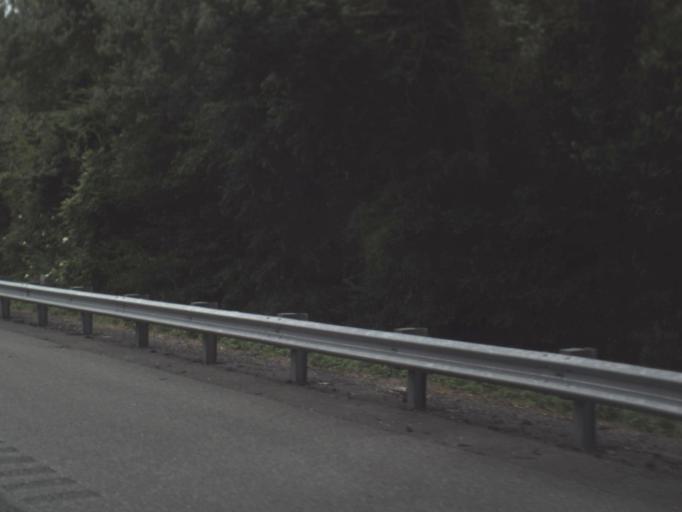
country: US
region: Florida
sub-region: Columbia County
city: Lake City
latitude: 30.0888
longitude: -82.6394
